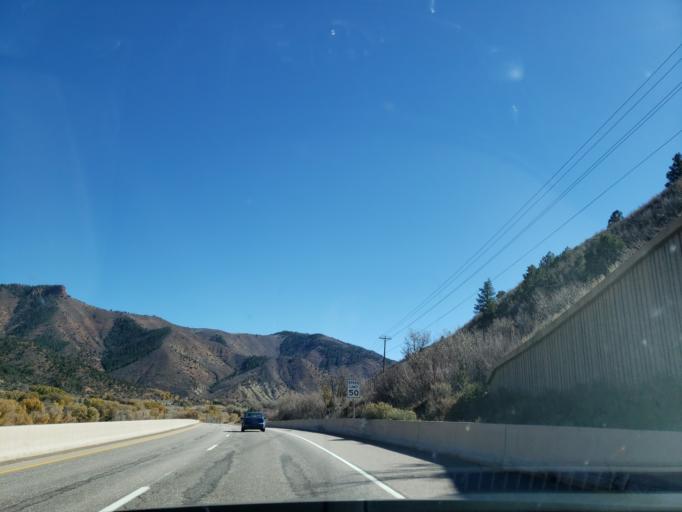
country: US
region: Colorado
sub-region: Eagle County
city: Basalt
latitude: 39.3268
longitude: -106.9578
